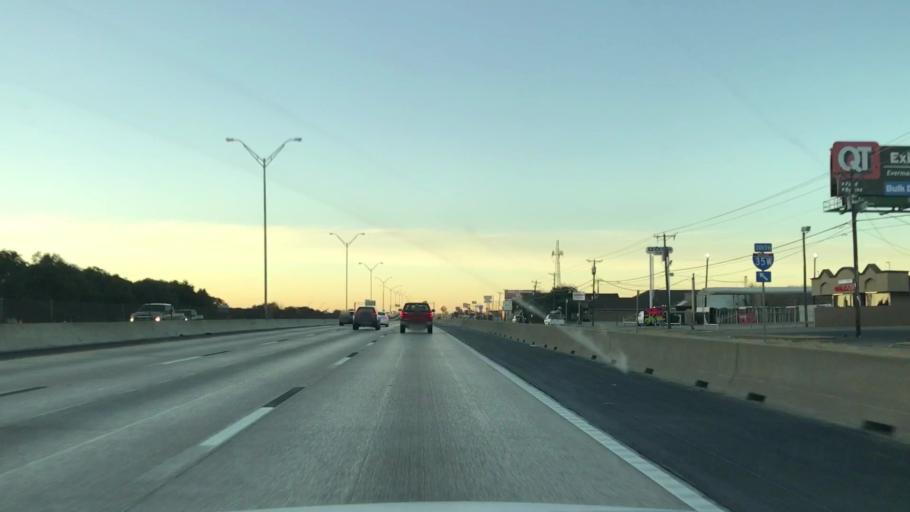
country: US
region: Texas
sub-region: Tarrant County
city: Edgecliff Village
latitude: 32.6426
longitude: -97.3215
